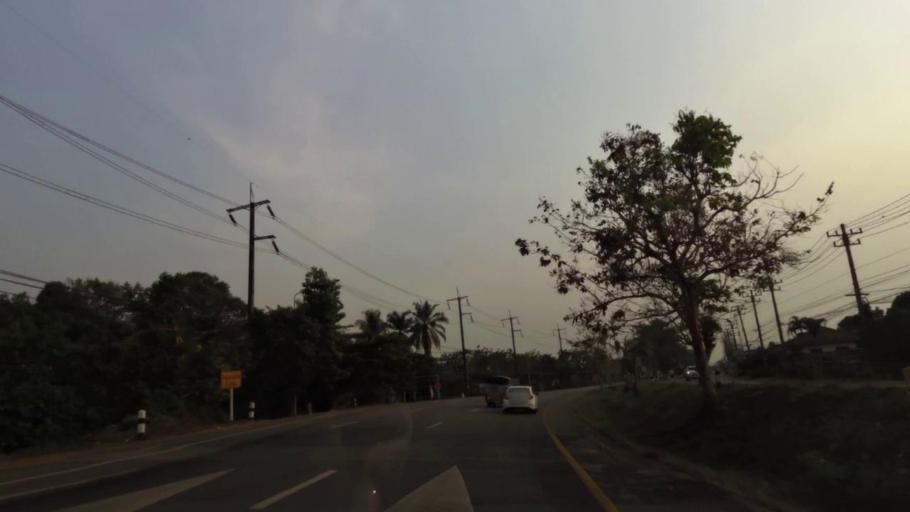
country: TH
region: Chanthaburi
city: Khlung
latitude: 12.5130
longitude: 102.1689
